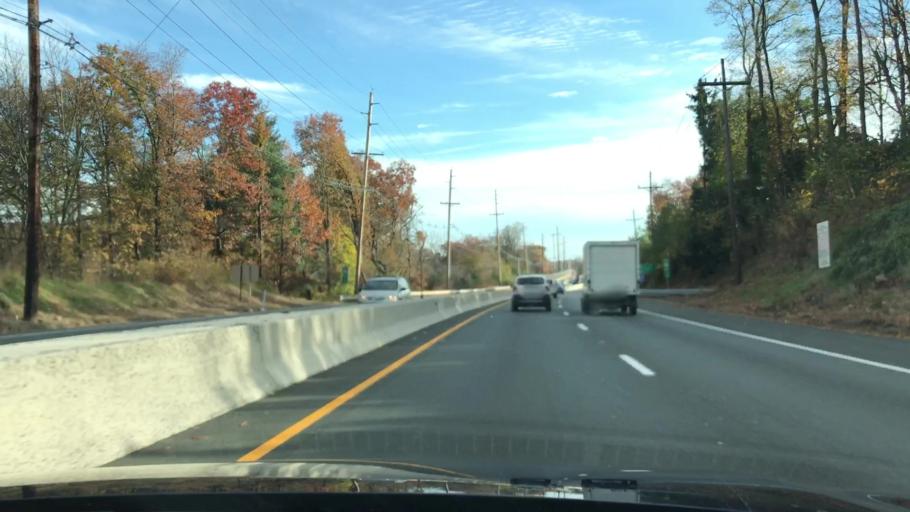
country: US
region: New Jersey
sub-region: Bergen County
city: Glen Rock
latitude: 40.9575
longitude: -74.1428
